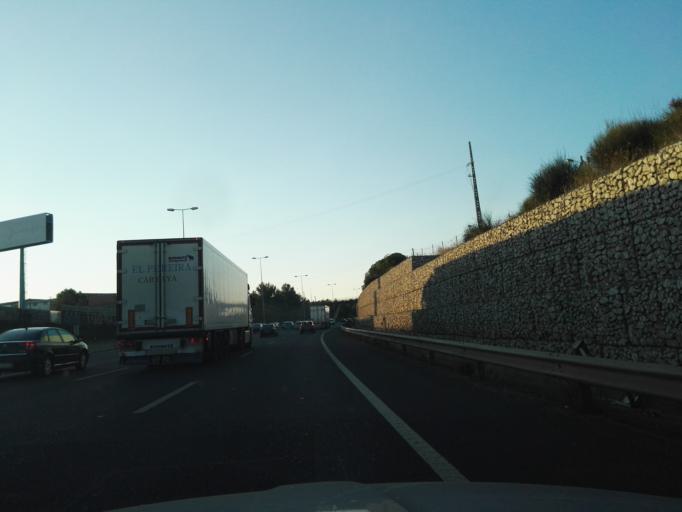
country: PT
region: Lisbon
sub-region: Loures
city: Camarate
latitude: 38.7964
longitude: -9.1212
